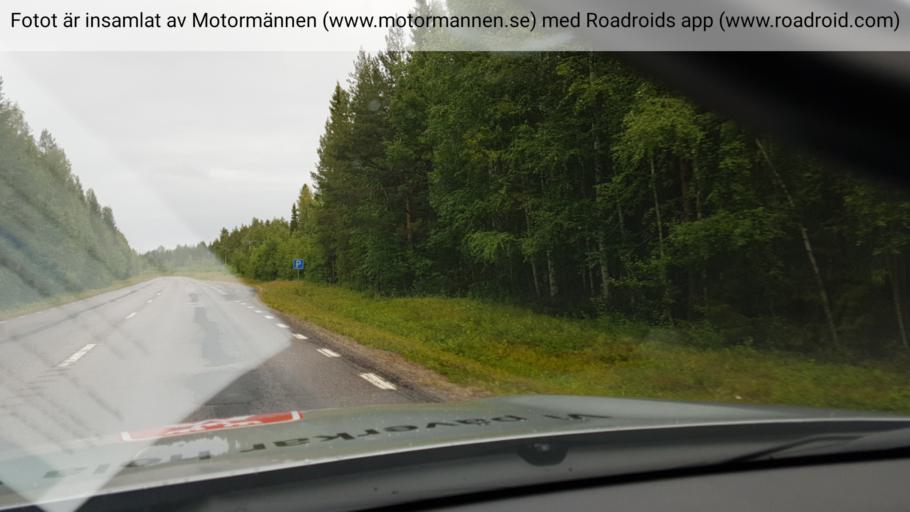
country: SE
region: Norrbotten
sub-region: Alvsbyns Kommun
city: AElvsbyn
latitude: 66.1606
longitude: 20.8797
